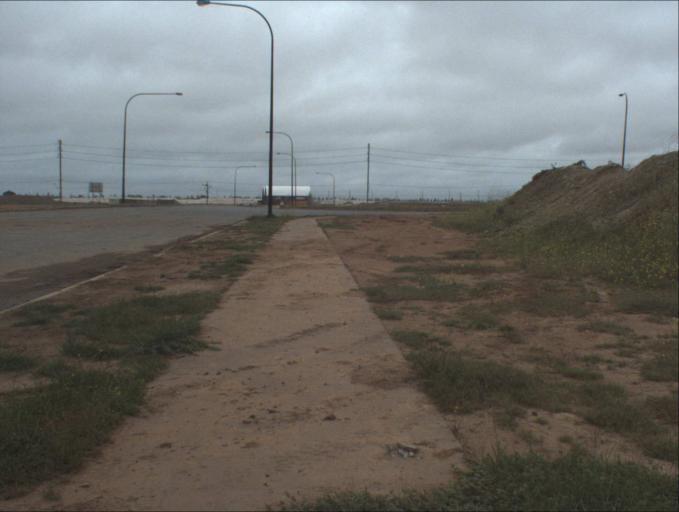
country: AU
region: South Australia
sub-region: Port Adelaide Enfield
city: Birkenhead
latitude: -34.8193
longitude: 138.5268
